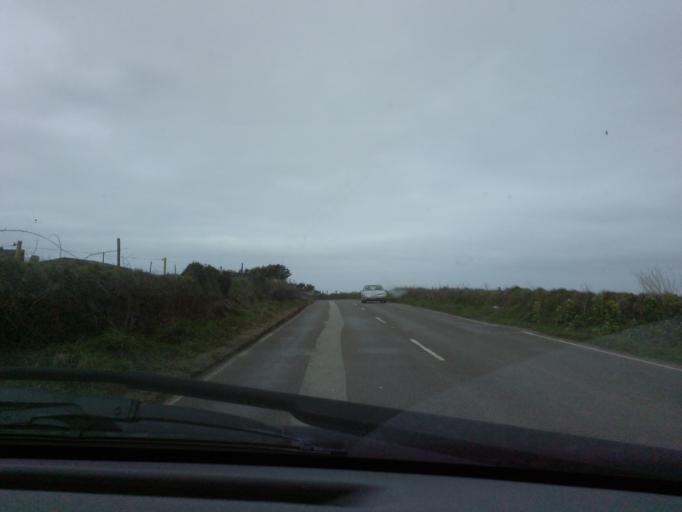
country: GB
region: England
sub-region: Cornwall
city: Saint Just
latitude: 50.1209
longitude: -5.6713
